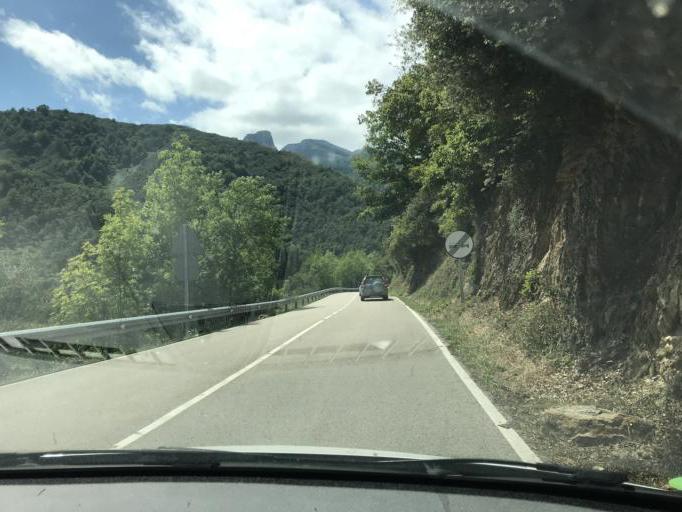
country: ES
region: Cantabria
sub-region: Provincia de Cantabria
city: Cabezon de Liebana
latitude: 43.0756
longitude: -4.5241
